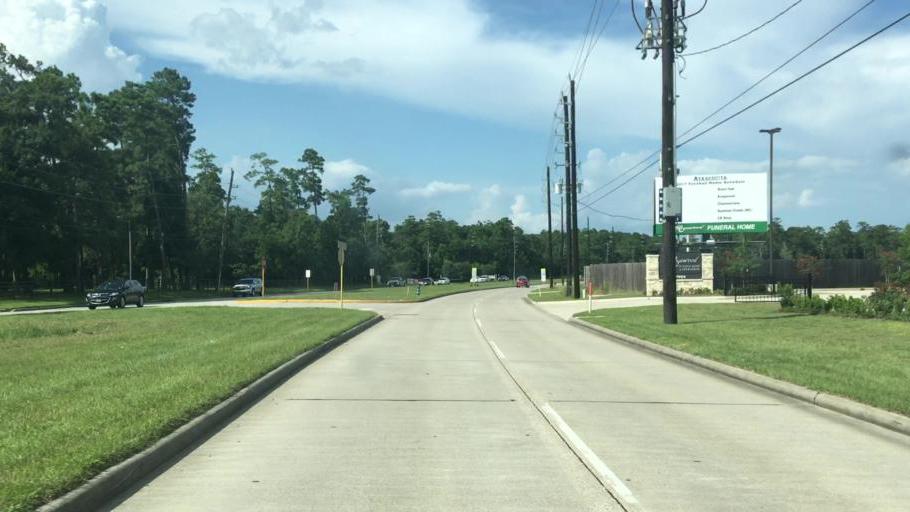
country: US
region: Texas
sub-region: Harris County
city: Atascocita
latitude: 29.9754
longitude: -95.1711
